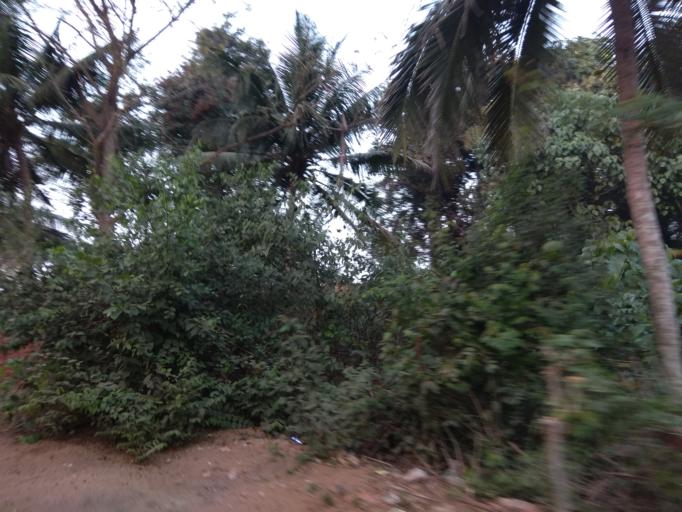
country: IN
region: Karnataka
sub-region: Dakshina Kannada
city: Mangalore
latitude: 12.9345
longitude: 74.8667
